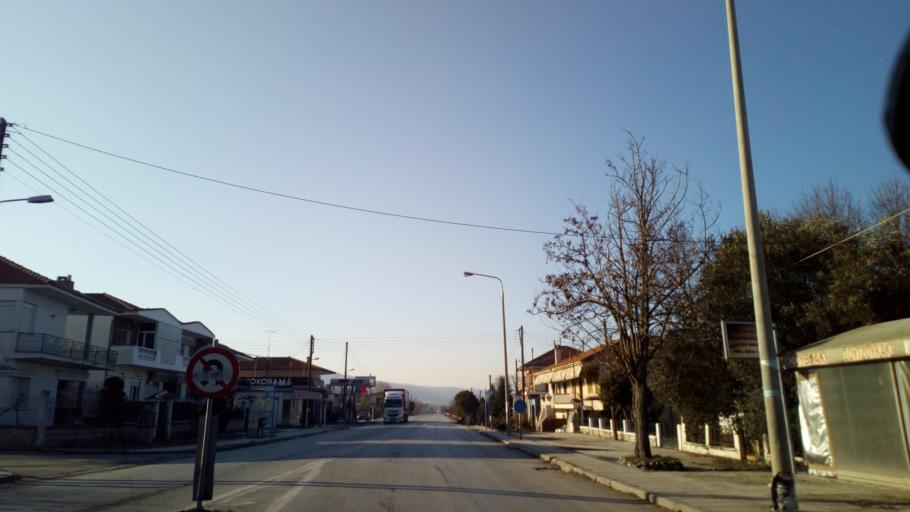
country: GR
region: Central Macedonia
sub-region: Nomos Thessalonikis
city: Agios Vasileios
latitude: 40.6648
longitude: 23.1134
